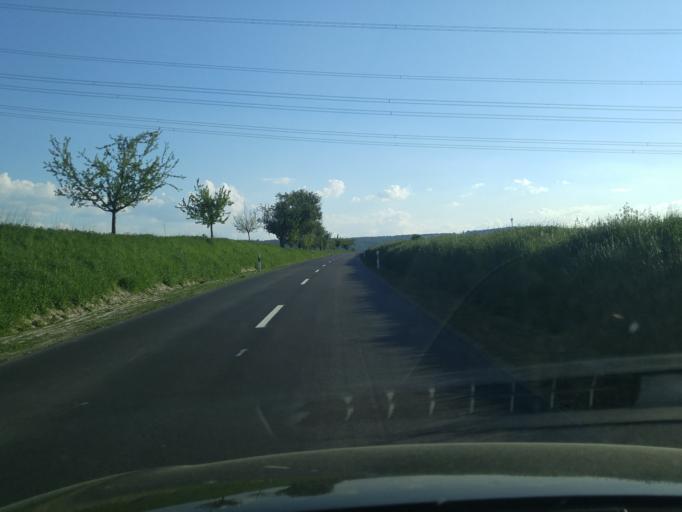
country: DE
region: Baden-Wuerttemberg
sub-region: Regierungsbezirk Stuttgart
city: Brackenheim
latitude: 49.0607
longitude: 9.0534
